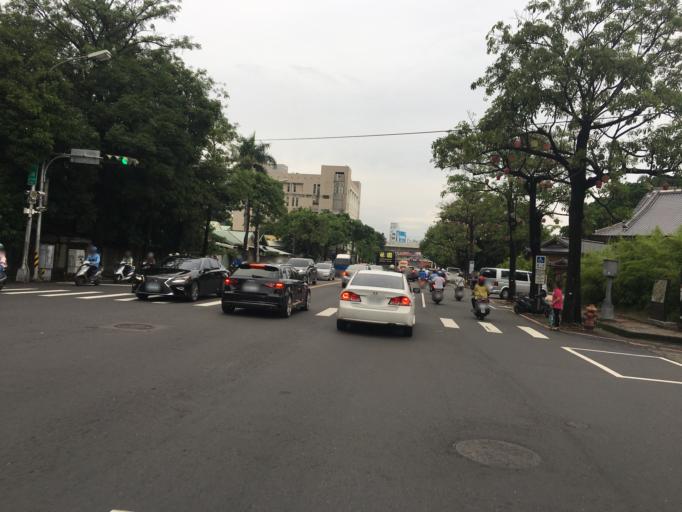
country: TW
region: Taiwan
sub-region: Taichung City
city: Taichung
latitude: 24.1350
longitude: 120.6736
